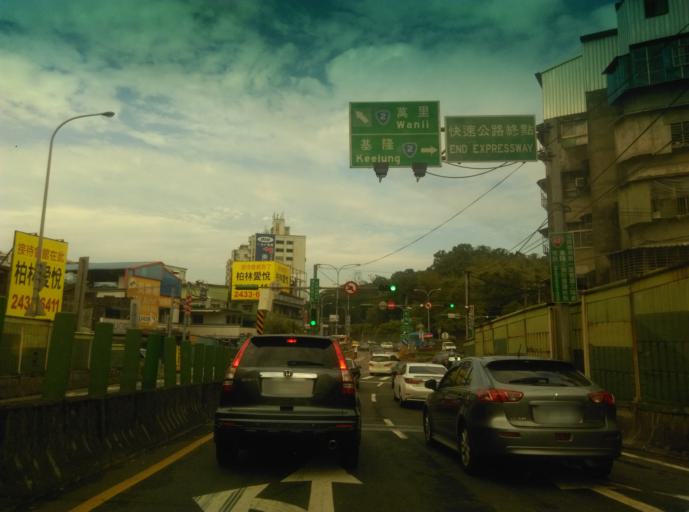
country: TW
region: Taiwan
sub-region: Keelung
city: Keelung
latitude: 25.1415
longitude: 121.7034
